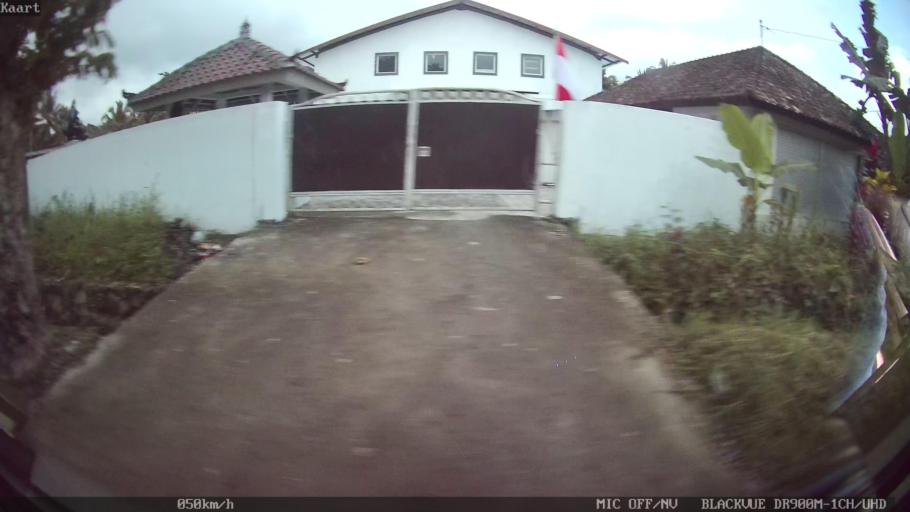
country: ID
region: Bali
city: Pohgending Kawan
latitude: -8.4489
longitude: 115.1398
